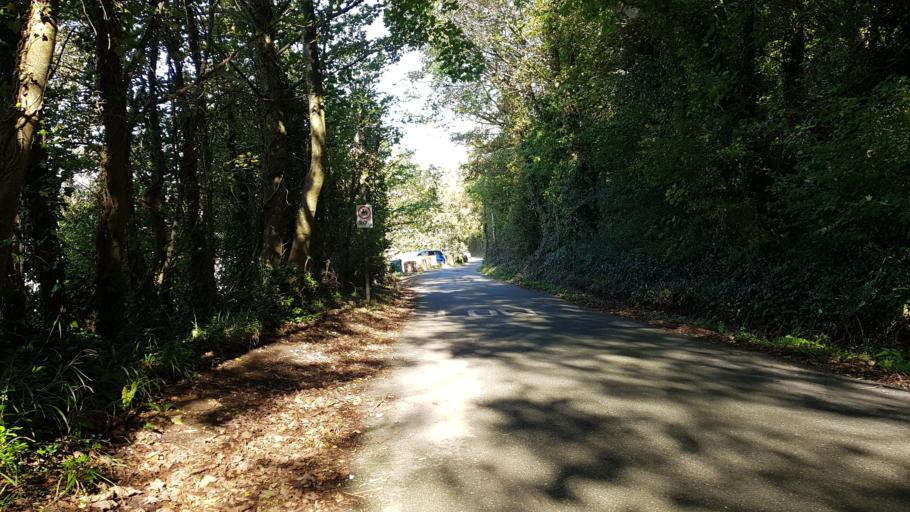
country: GB
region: England
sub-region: Isle of Wight
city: Newport
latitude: 50.6882
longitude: -1.2866
